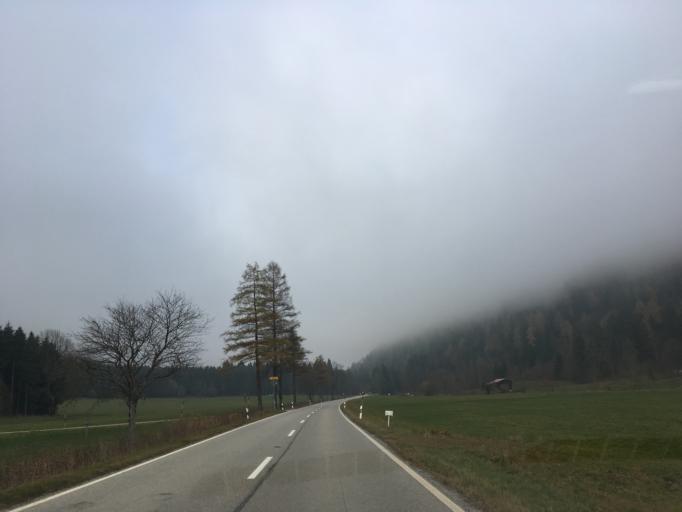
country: AT
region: Tyrol
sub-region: Politischer Bezirk Kufstein
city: Rettenschoss
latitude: 47.7062
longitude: 12.2792
